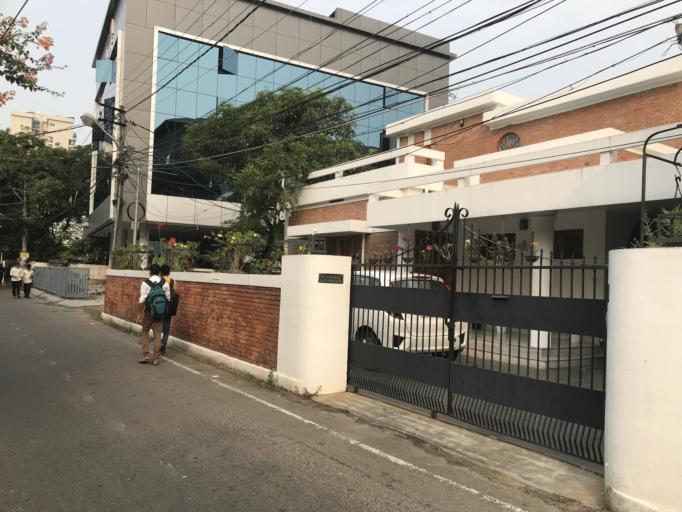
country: IN
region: Kerala
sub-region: Ernakulam
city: Cochin
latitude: 9.9979
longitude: 76.2926
